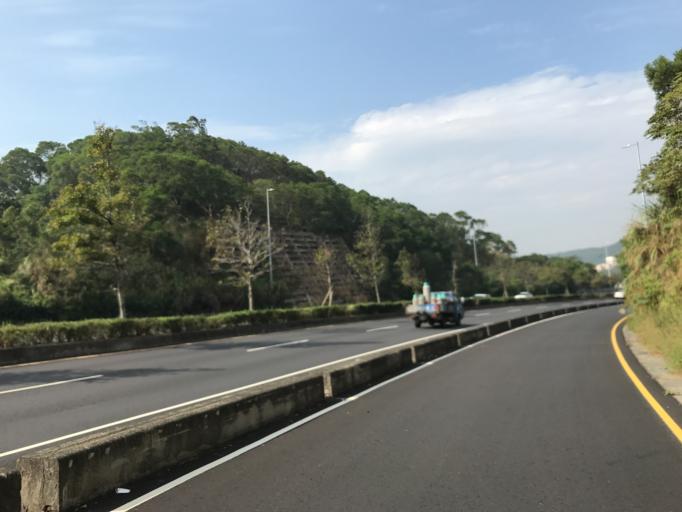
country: TW
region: Taiwan
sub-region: Hsinchu
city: Hsinchu
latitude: 24.7694
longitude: 120.9527
